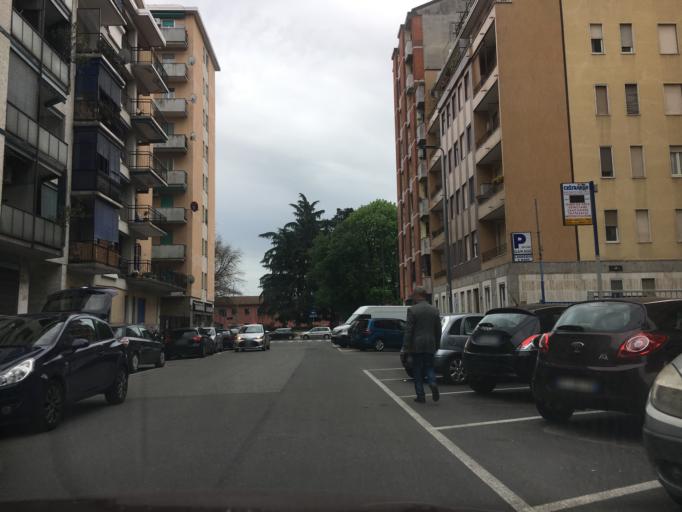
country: IT
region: Lombardy
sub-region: Citta metropolitana di Milano
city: Romano Banco
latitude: 45.4488
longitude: 9.1382
